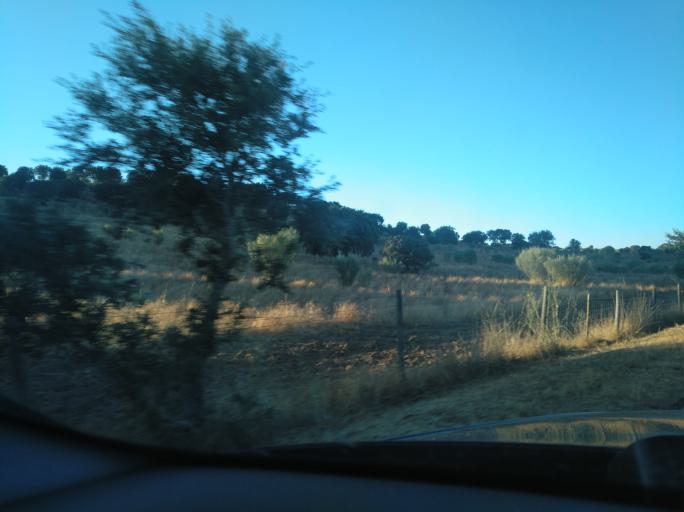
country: PT
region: Portalegre
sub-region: Arronches
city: Arronches
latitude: 39.0697
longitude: -7.2419
